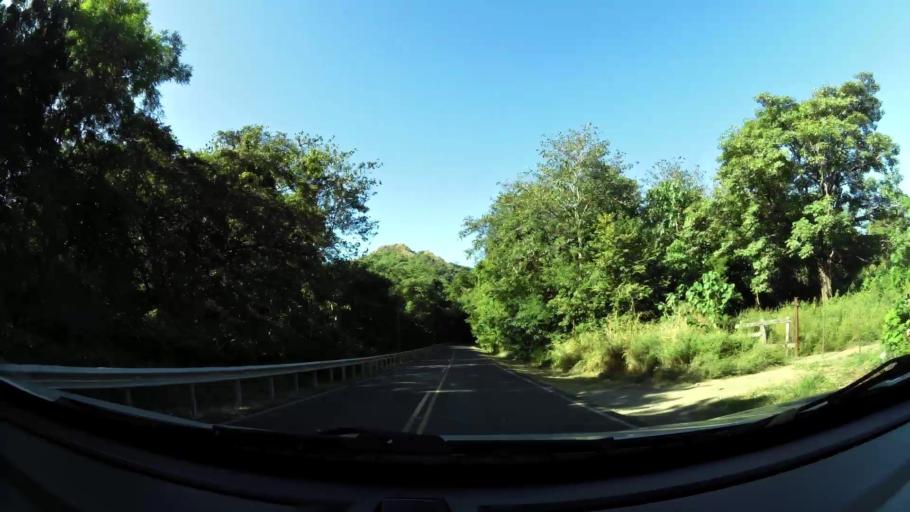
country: CR
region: Guanacaste
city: Belen
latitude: 10.3704
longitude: -85.6328
